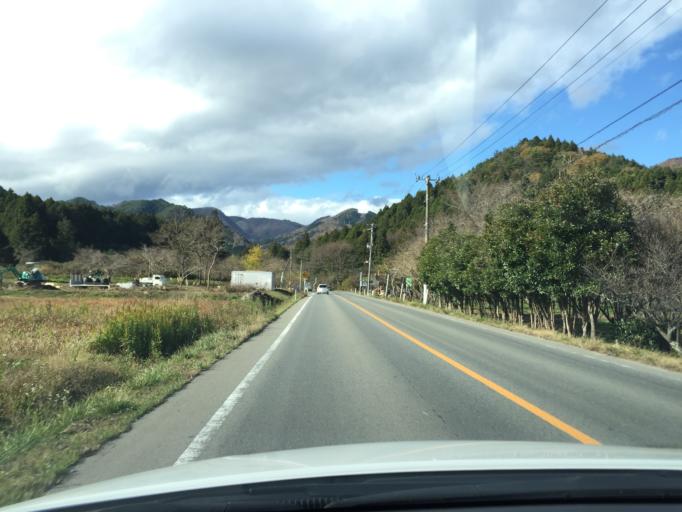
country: JP
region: Fukushima
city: Namie
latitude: 37.6643
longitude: 140.8888
